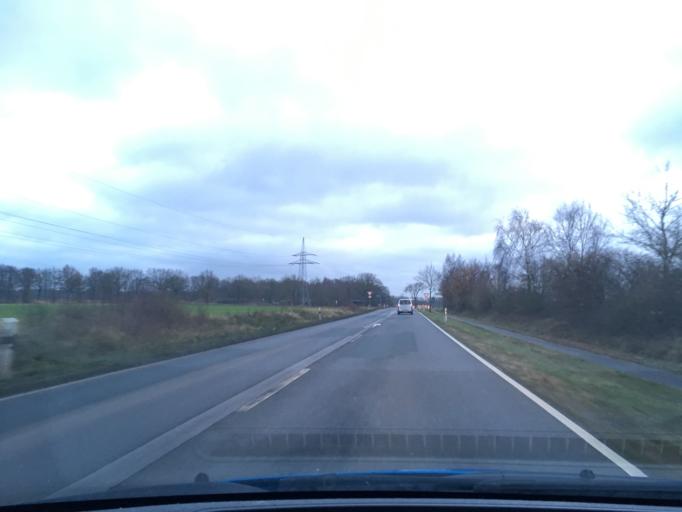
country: DE
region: Lower Saxony
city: Winsen
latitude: 53.3291
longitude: 10.2147
